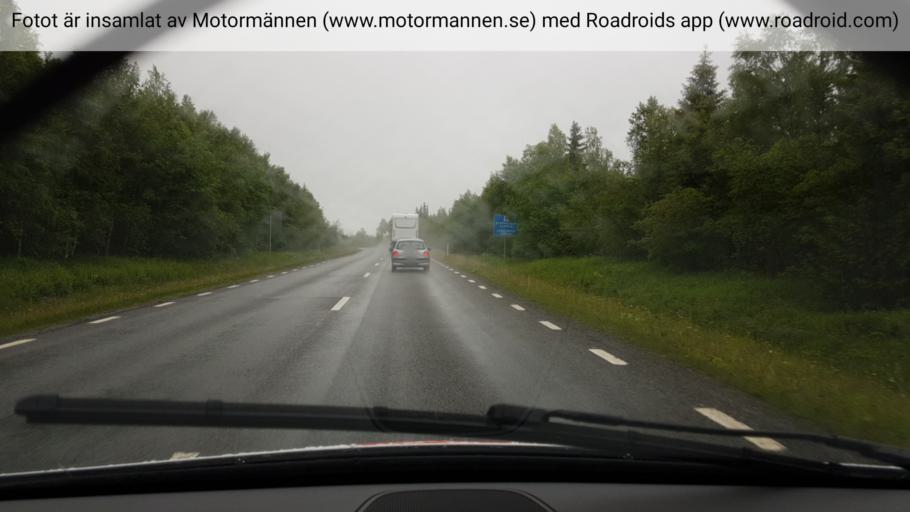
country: SE
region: Jaemtland
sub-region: OEstersunds Kommun
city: Lit
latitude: 63.4580
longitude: 15.1754
